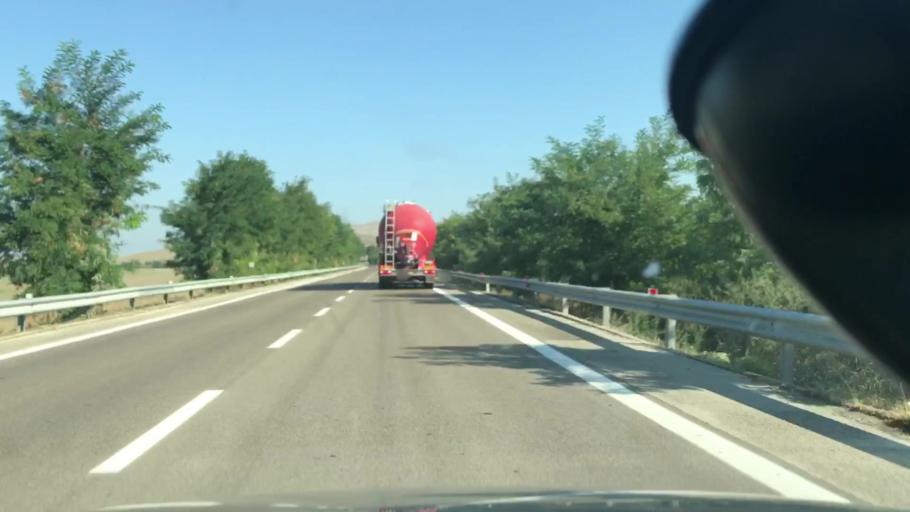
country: IT
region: Basilicate
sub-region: Provincia di Matera
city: Irsina
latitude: 40.8011
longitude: 16.2744
